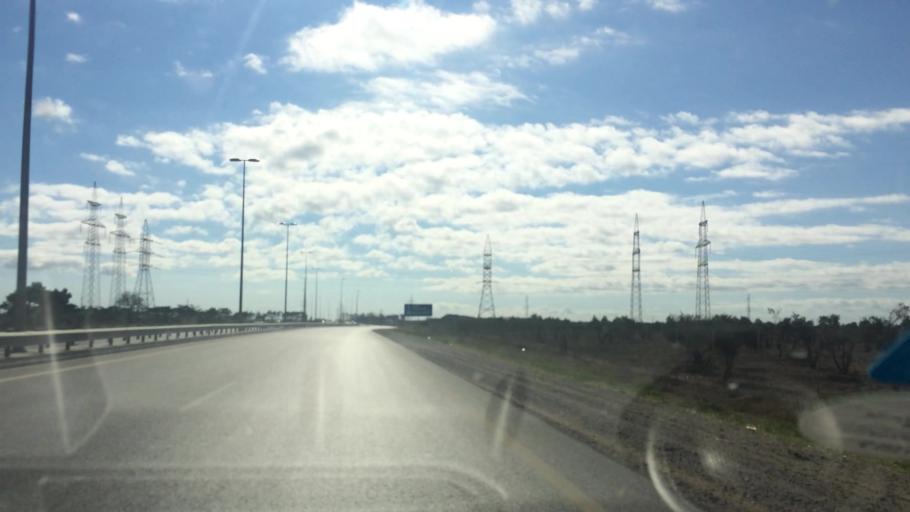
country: AZ
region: Baki
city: Qala
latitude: 40.4387
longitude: 50.1828
